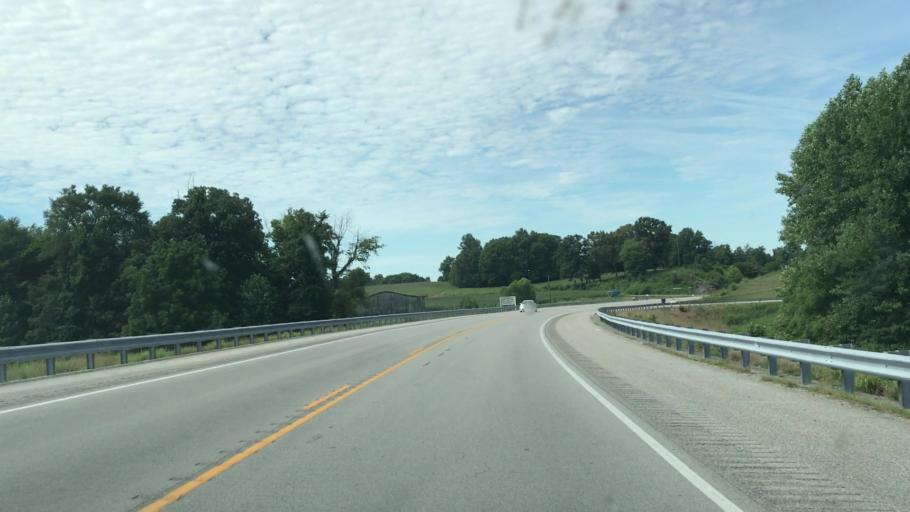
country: US
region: Kentucky
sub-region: Edmonson County
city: Brownsville
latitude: 37.1483
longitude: -86.2213
